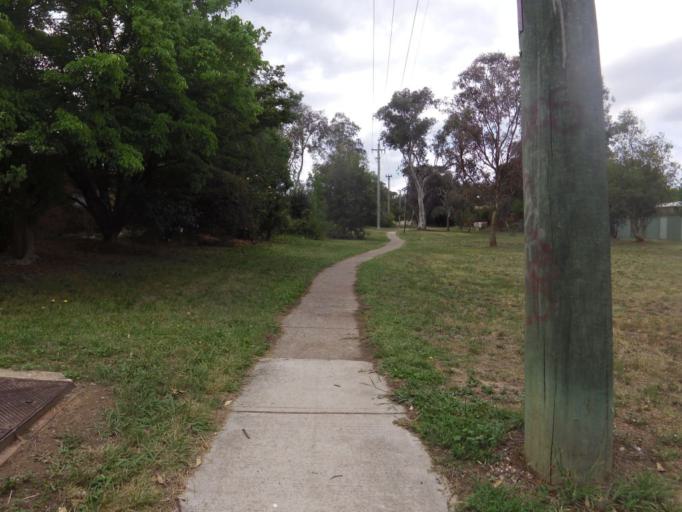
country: AU
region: Australian Capital Territory
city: Macarthur
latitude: -35.4070
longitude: 149.1281
